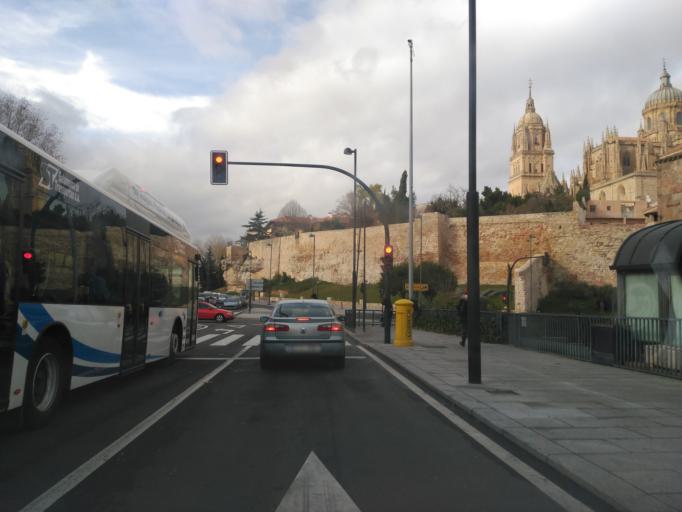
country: ES
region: Castille and Leon
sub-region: Provincia de Salamanca
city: Salamanca
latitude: 40.9589
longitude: -5.6642
